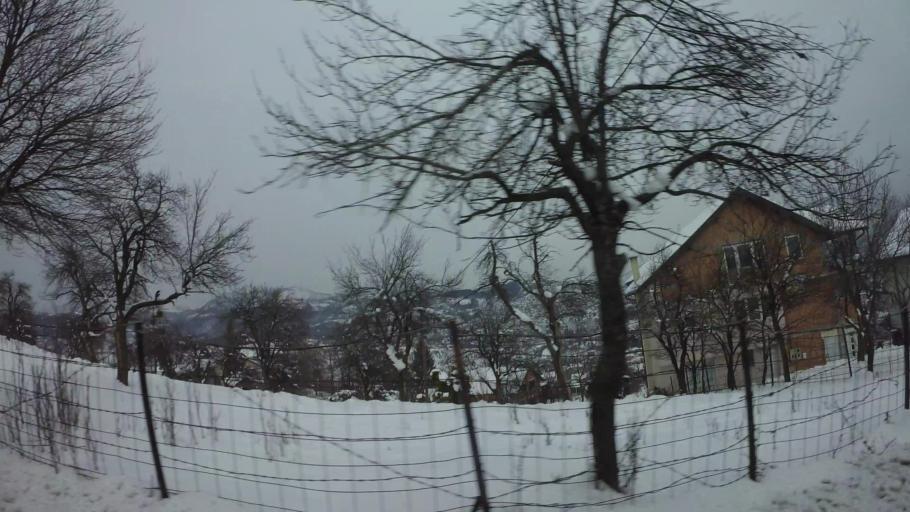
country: BA
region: Federation of Bosnia and Herzegovina
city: Kobilja Glava
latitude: 43.8713
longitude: 18.3956
